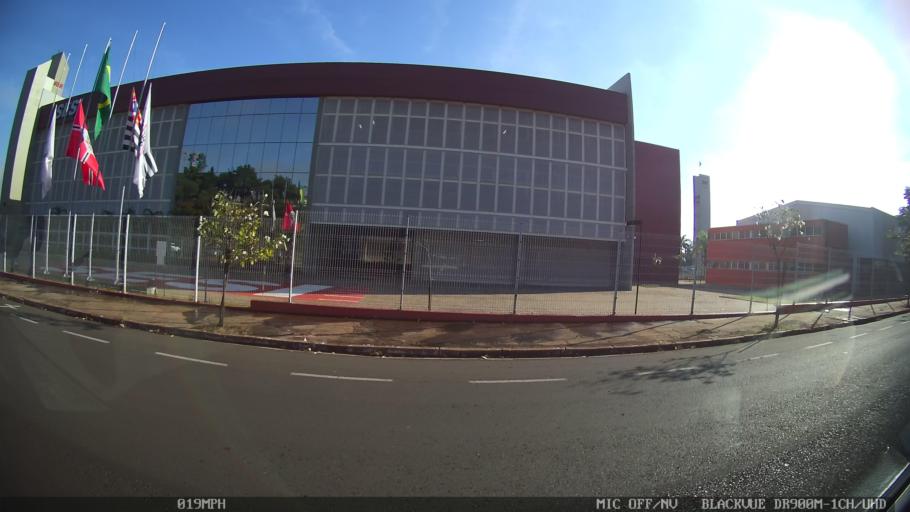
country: BR
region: Sao Paulo
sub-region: Sao Jose Do Rio Preto
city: Sao Jose do Rio Preto
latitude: -20.8104
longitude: -49.3633
